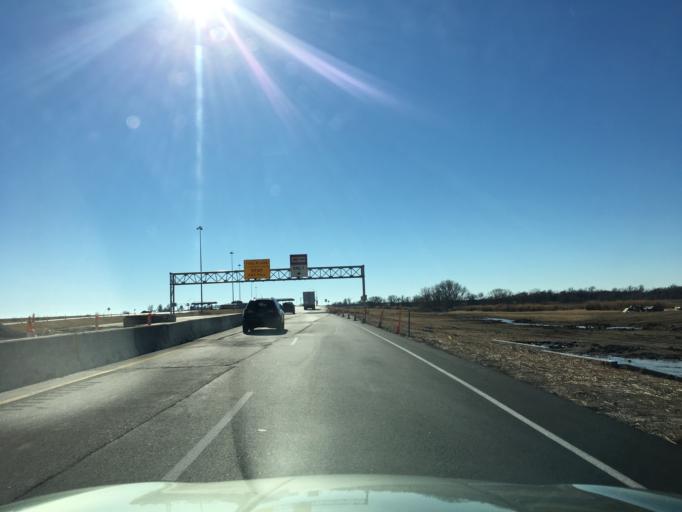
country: US
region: Kansas
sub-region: Sumner County
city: Wellington
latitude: 37.2439
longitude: -97.3391
